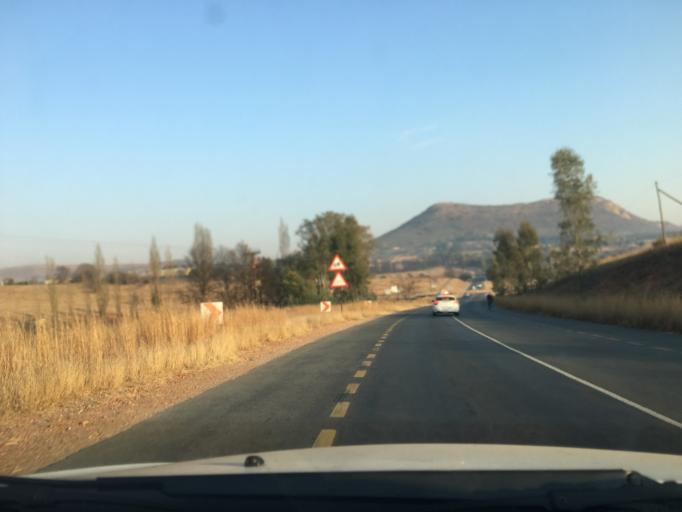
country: ZA
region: Gauteng
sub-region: West Rand District Municipality
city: Muldersdriseloop
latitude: -25.9927
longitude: 27.8485
